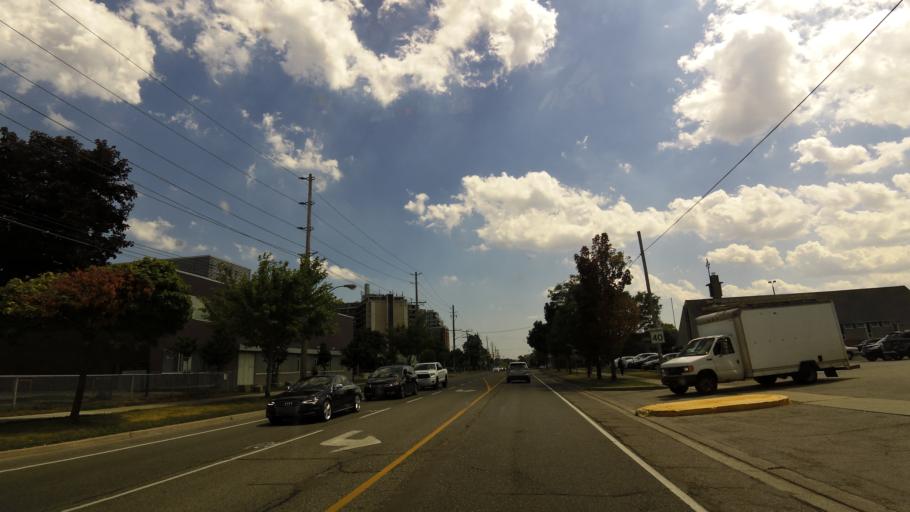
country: CA
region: Ontario
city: Etobicoke
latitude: 43.6857
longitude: -79.5281
